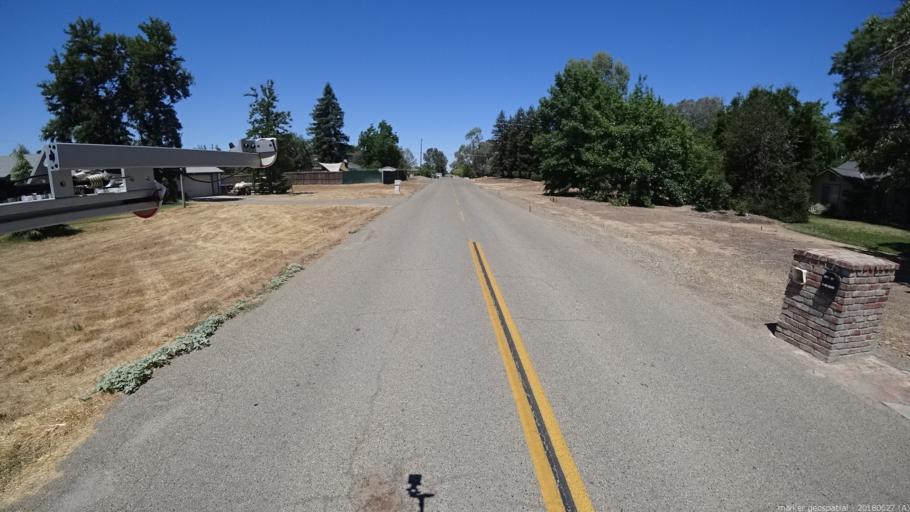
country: US
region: California
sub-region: Madera County
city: Bonadelle Ranchos-Madera Ranchos
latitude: 36.9330
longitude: -119.8764
